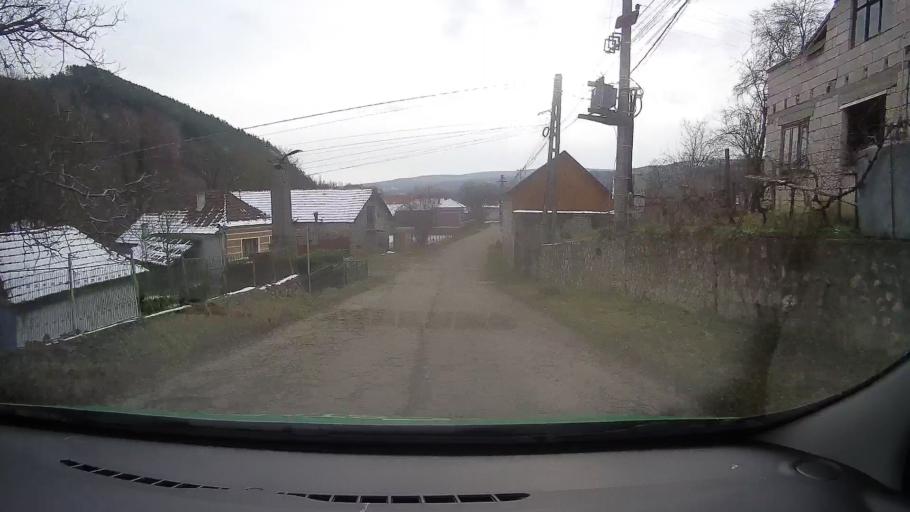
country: RO
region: Hunedoara
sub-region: Comuna Geoagiu
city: Geoagiu
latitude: 45.9713
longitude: 23.1709
